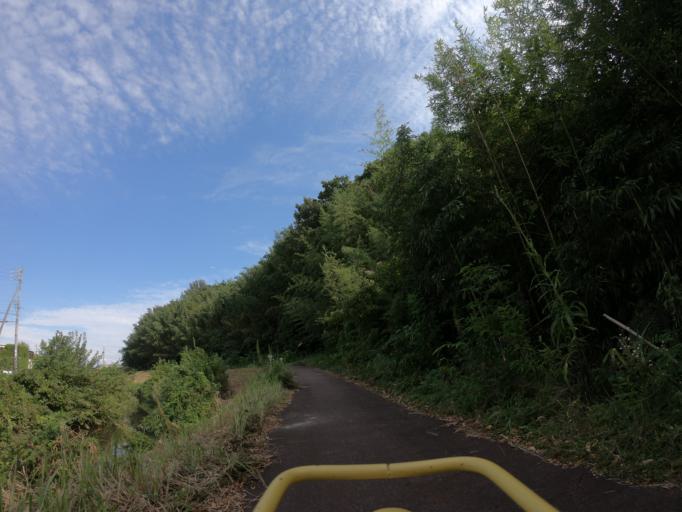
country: JP
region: Aichi
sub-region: Toyota-shi
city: Toyota
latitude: 35.1301
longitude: 137.0533
